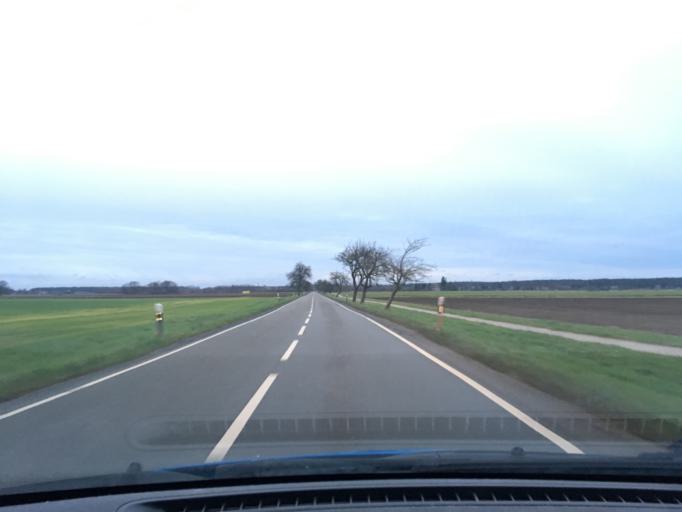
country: DE
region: Lower Saxony
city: Neu Darchau
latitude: 53.2660
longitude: 10.9217
